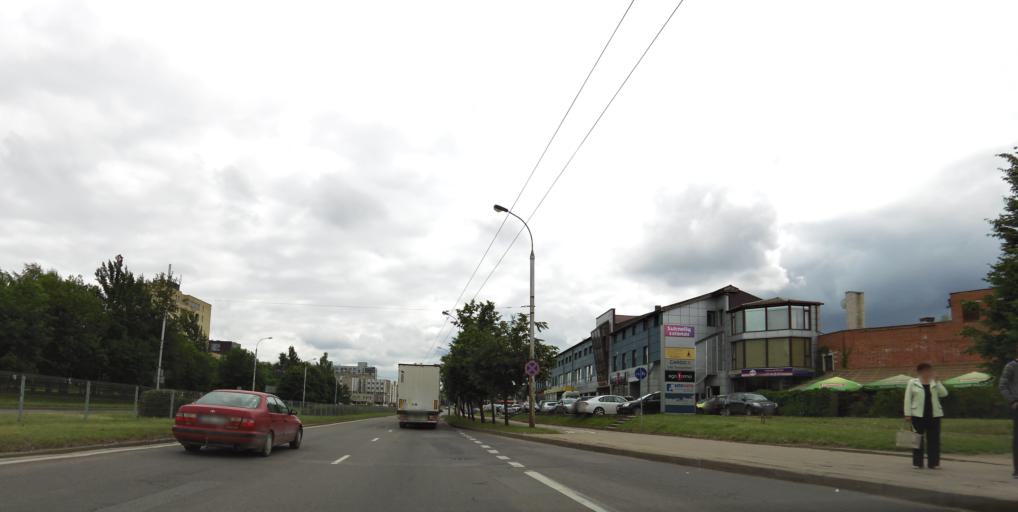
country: LT
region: Vilnius County
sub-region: Vilnius
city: Fabijoniskes
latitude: 54.7257
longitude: 25.2335
